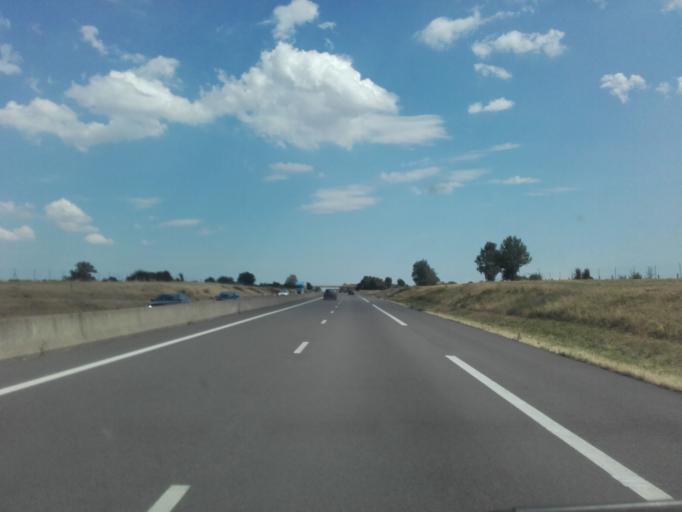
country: FR
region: Bourgogne
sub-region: Departement de la Cote-d'Or
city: Semur-en-Auxois
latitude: 47.4766
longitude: 4.1975
